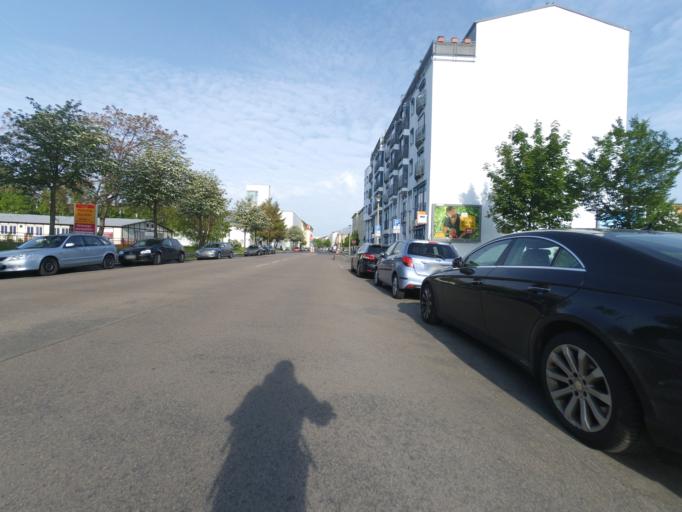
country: DE
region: Saxony
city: Dresden
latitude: 51.0518
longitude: 13.7628
